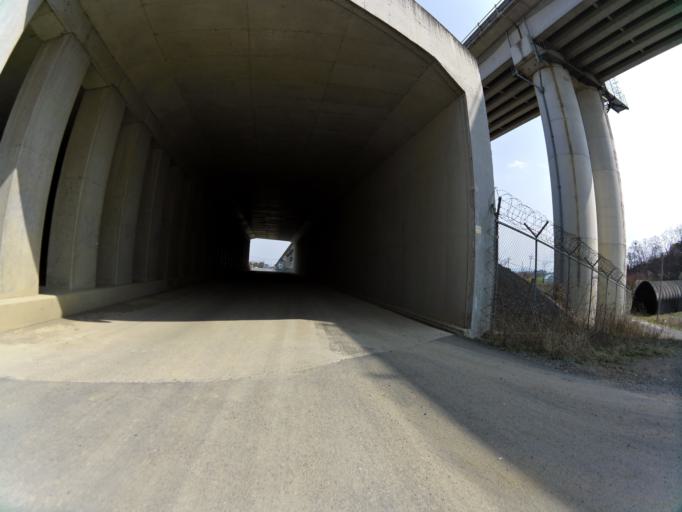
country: KR
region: Gyeongsangbuk-do
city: Gyeongsan-si
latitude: 35.8539
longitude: 128.7165
